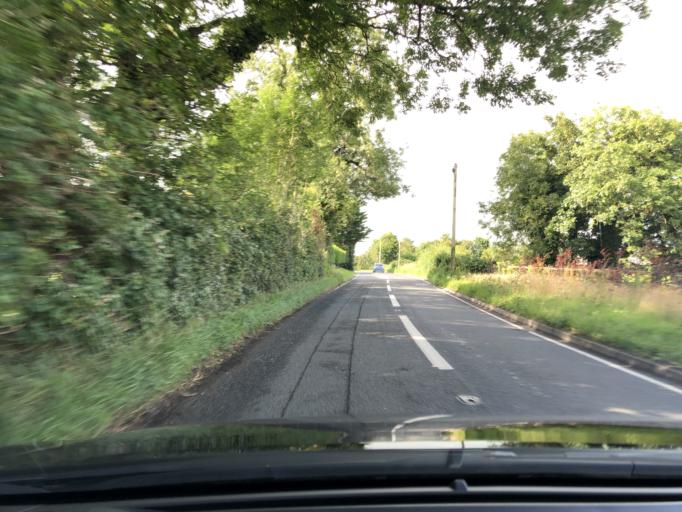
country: GB
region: Northern Ireland
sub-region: Down District
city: Dundrum
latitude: 54.2831
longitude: -5.8112
